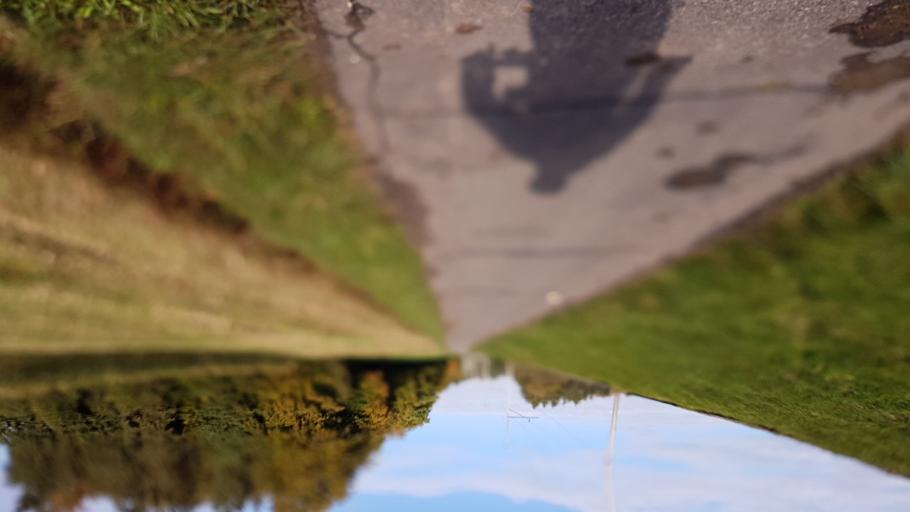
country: CH
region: Bern
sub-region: Bern-Mittelland District
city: Worb
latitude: 46.9218
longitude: 7.5429
